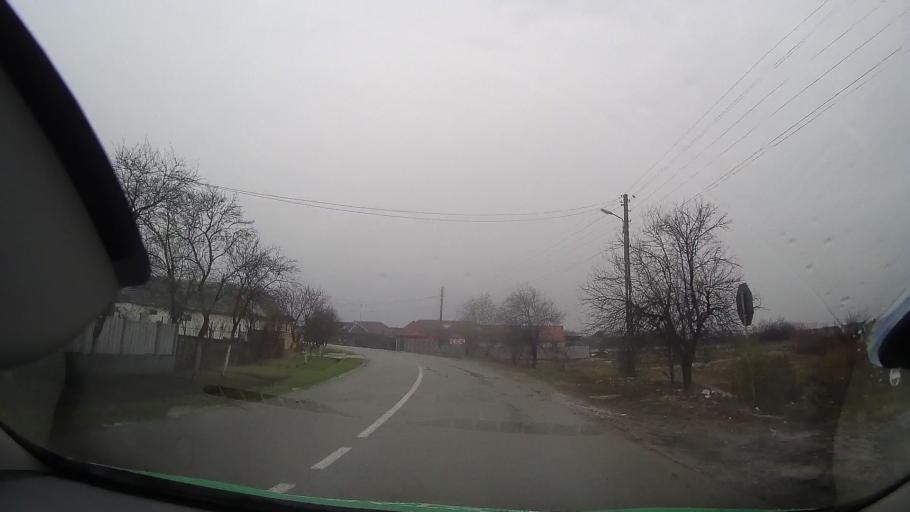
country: RO
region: Bihor
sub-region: Comuna Tulca
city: Tulca
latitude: 46.7935
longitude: 21.7636
